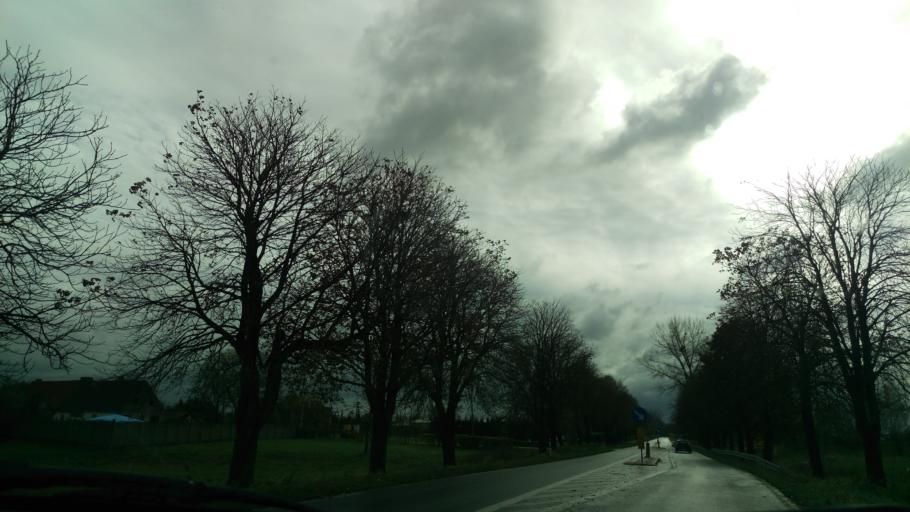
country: PL
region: West Pomeranian Voivodeship
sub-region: Powiat gryficki
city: Ploty
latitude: 53.8222
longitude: 15.2514
